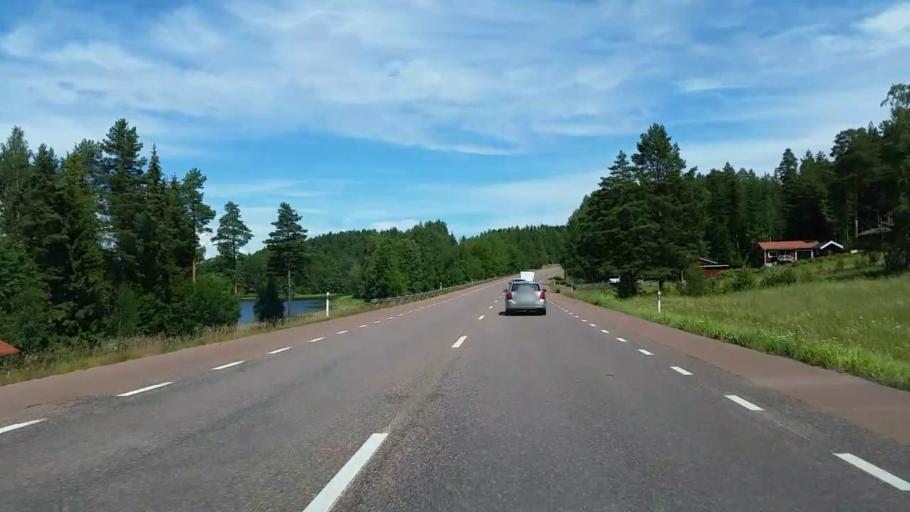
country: SE
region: Dalarna
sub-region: Rattviks Kommun
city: Raettvik
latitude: 60.9211
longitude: 15.2094
